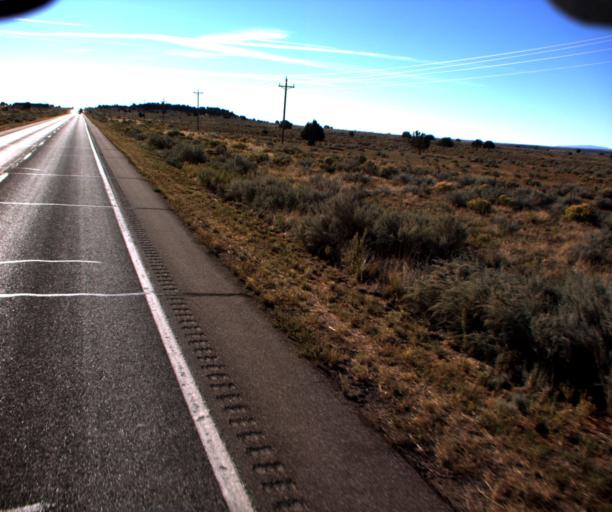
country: US
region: Arizona
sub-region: Mohave County
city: Colorado City
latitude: 36.9774
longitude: -112.9805
